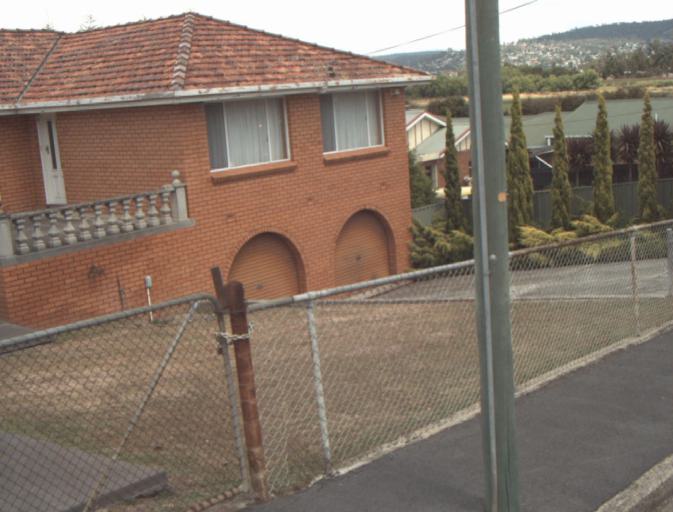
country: AU
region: Tasmania
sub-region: Launceston
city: Newnham
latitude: -41.4128
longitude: 147.1496
